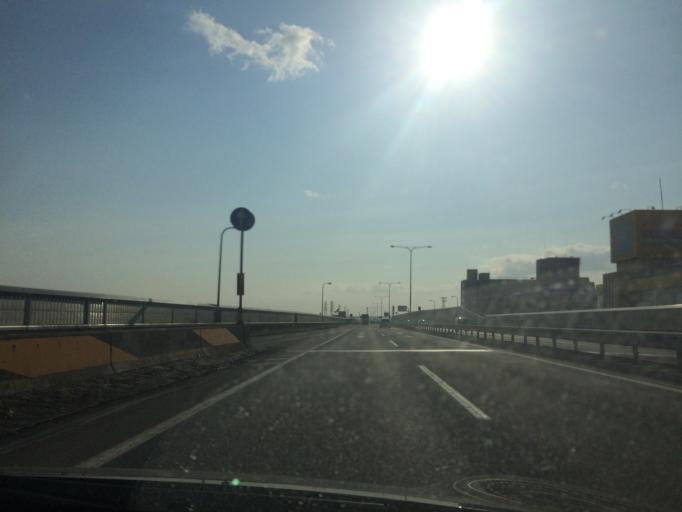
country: JP
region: Hokkaido
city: Sapporo
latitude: 43.0975
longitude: 141.3933
